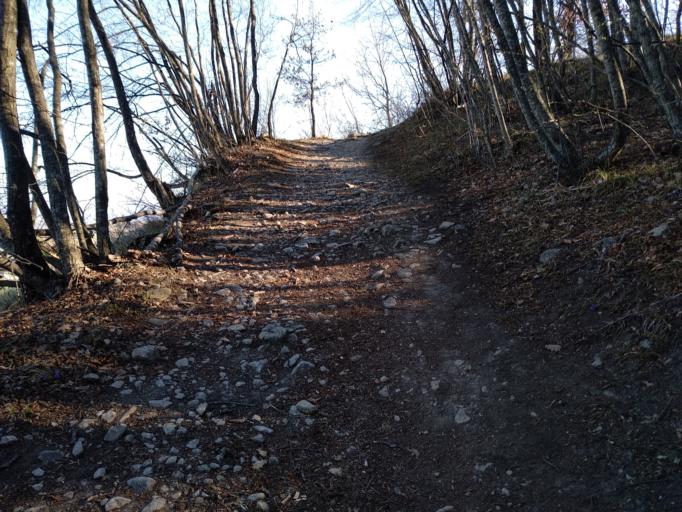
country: IT
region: Emilia-Romagna
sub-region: Provincia di Reggio Emilia
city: Castelnovo ne'Monti
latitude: 44.4221
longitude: 10.4196
